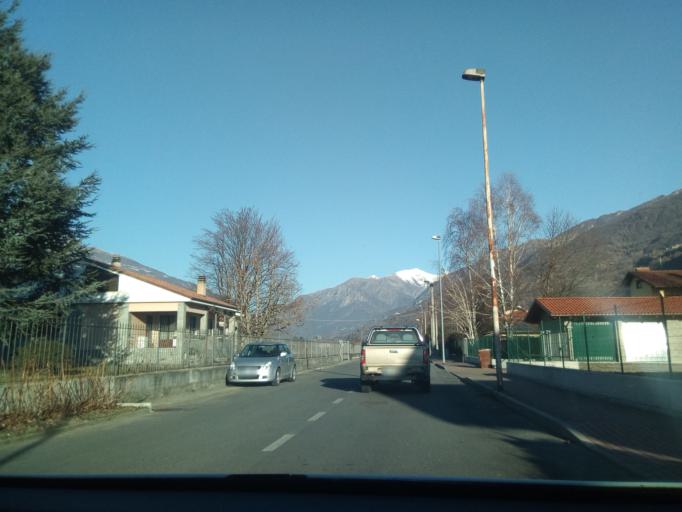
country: IT
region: Piedmont
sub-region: Provincia di Torino
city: Borgofranco d'Ivrea
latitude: 45.5170
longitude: 7.8572
